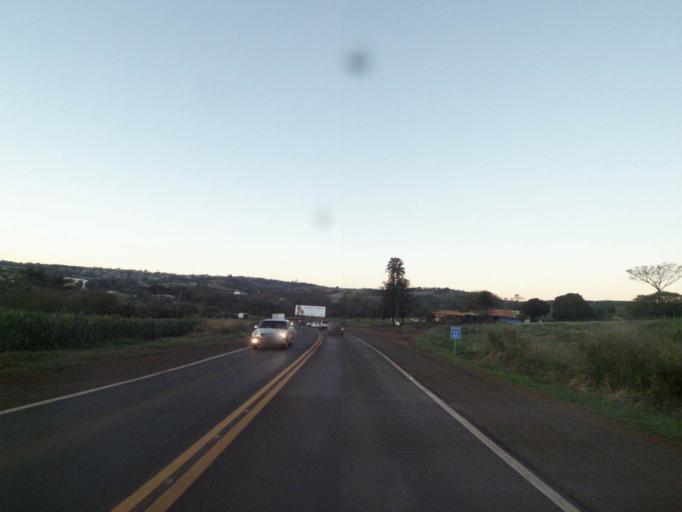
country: BR
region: Parana
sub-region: Londrina
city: Londrina
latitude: -23.4035
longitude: -51.1347
